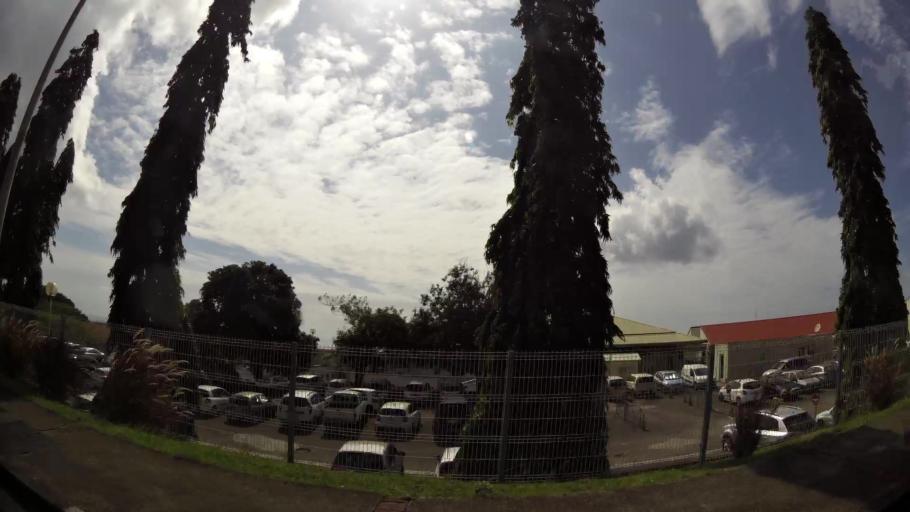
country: GP
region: Guadeloupe
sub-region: Guadeloupe
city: Basse-Terre
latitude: 16.0044
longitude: -61.7294
